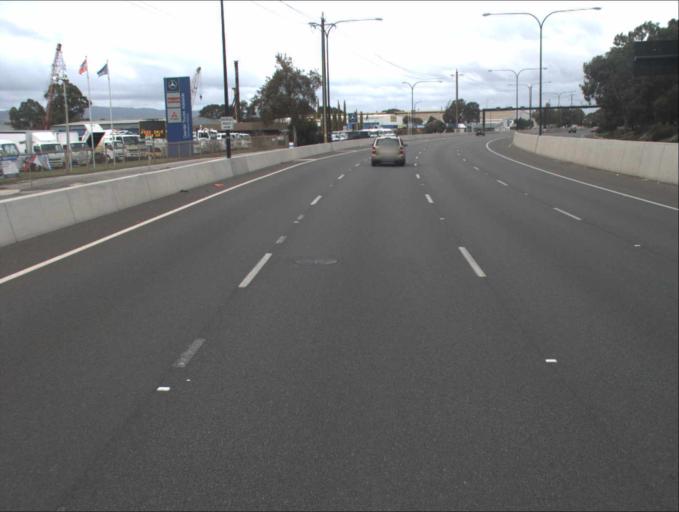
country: AU
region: South Australia
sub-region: Port Adelaide Enfield
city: Blair Athol
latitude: -34.8637
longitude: 138.5697
